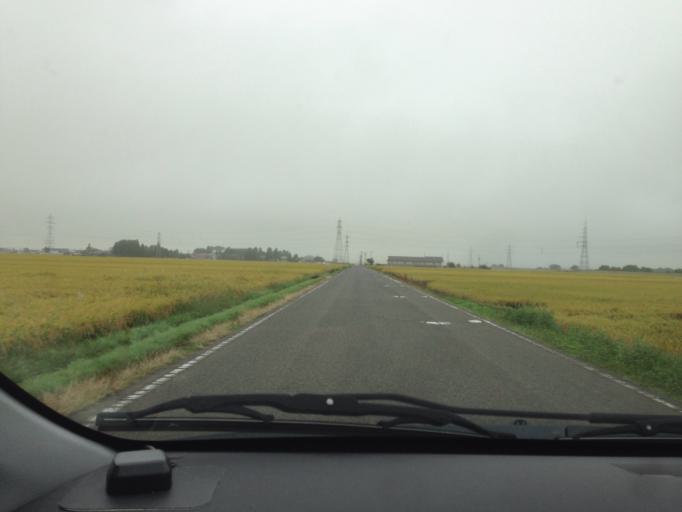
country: JP
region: Fukushima
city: Kitakata
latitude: 37.5810
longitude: 139.8658
